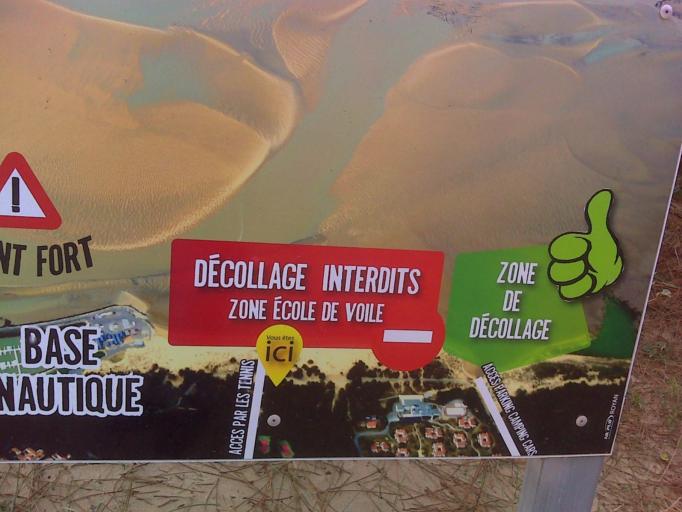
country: FR
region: Poitou-Charentes
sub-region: Departement de la Charente-Maritime
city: Les Mathes
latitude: 45.6869
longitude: -1.1876
